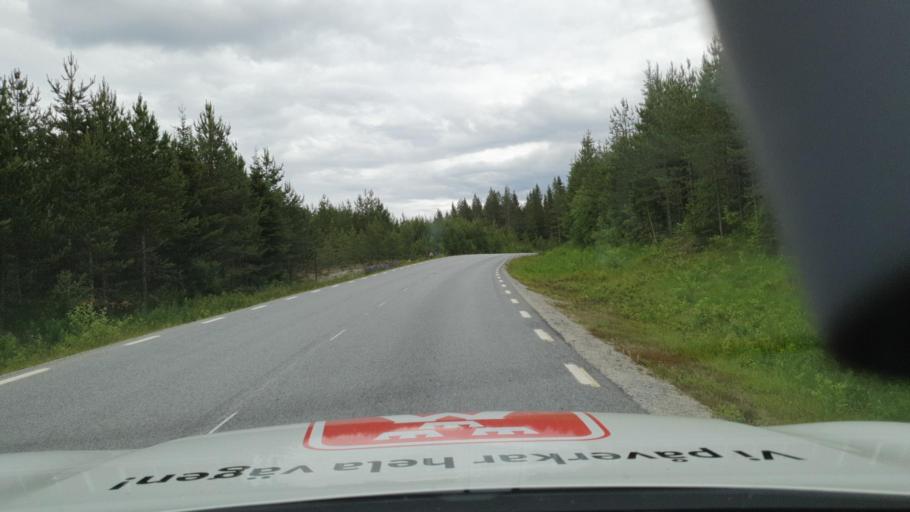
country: SE
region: Vaesterbotten
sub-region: Bjurholms Kommun
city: Bjurholm
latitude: 63.8839
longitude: 19.0265
